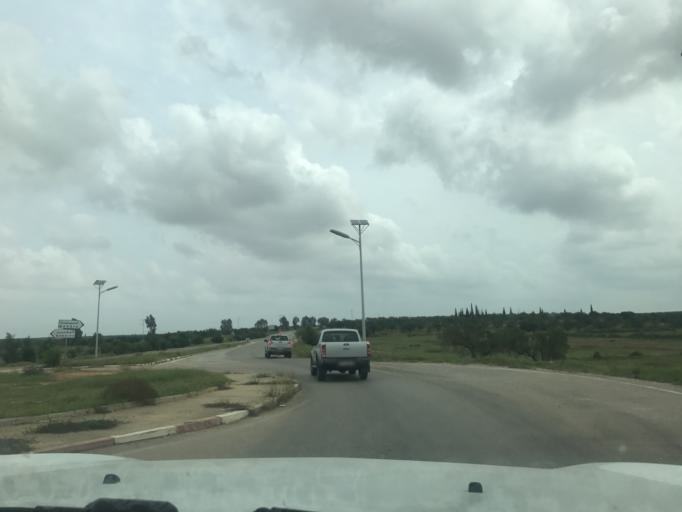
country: TN
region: Al Munastir
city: Sidi Bin Nur
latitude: 35.5441
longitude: 10.8762
